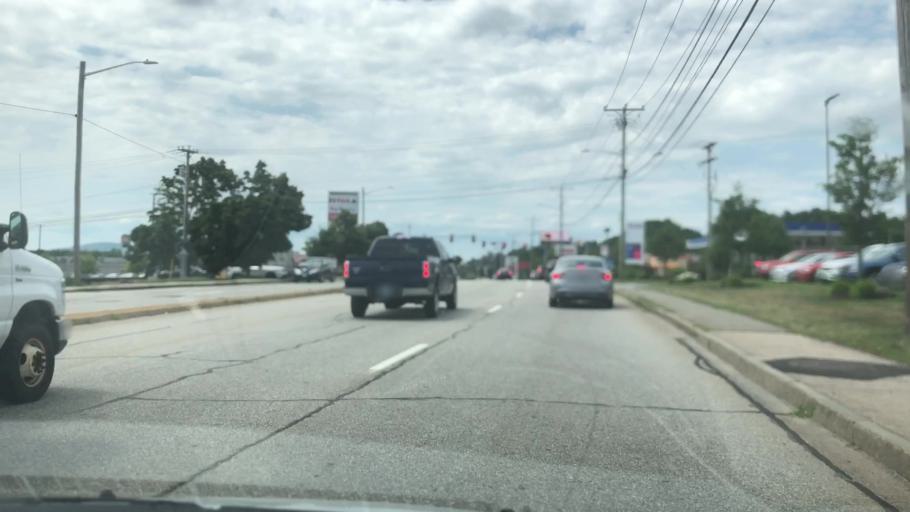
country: US
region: New Hampshire
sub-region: Hillsborough County
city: Manchester
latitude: 42.9612
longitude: -71.4385
